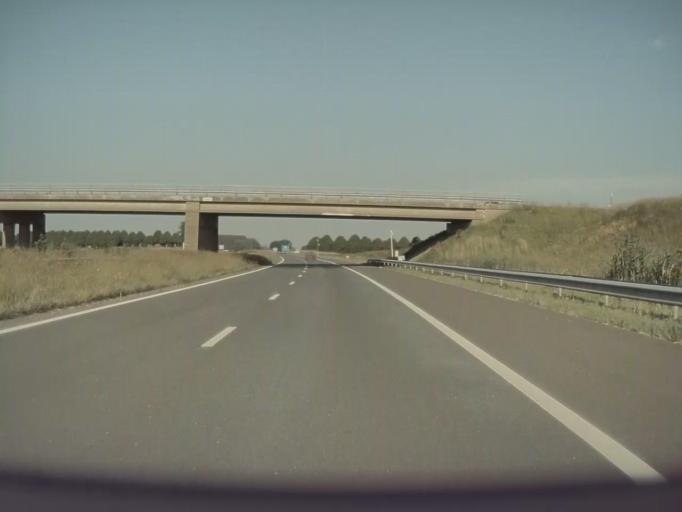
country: NL
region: North Brabant
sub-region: Gemeente Moerdijk
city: Klundert
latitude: 51.6366
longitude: 4.4997
